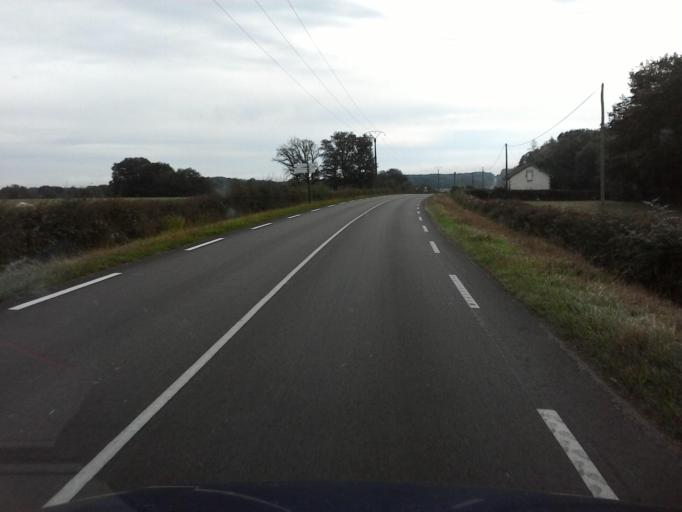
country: FR
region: Bourgogne
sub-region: Departement de Saone-et-Loire
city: Autun
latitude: 47.0041
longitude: 4.2067
